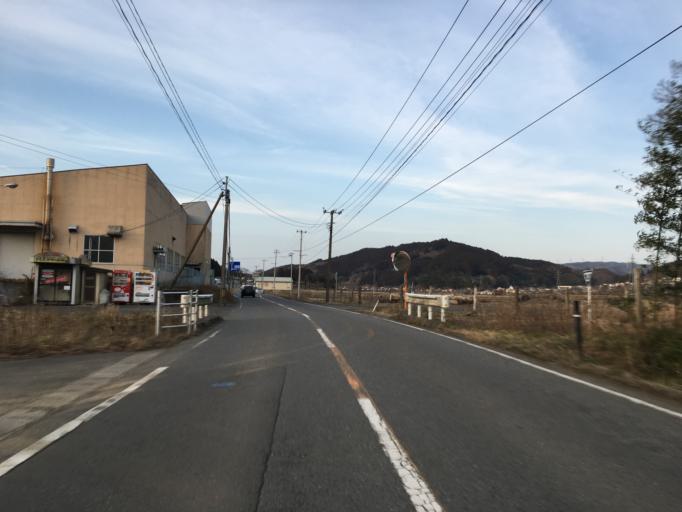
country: JP
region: Ibaraki
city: Daigo
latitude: 36.9425
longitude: 140.4064
